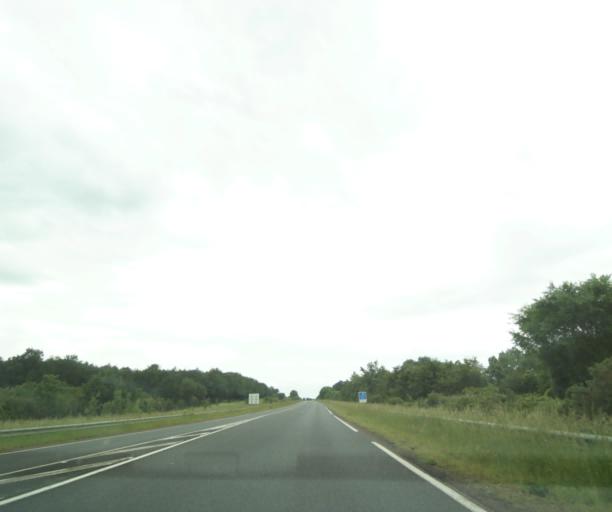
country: FR
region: Poitou-Charentes
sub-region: Departement des Deux-Sevres
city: Airvault
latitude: 46.7992
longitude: -0.2128
